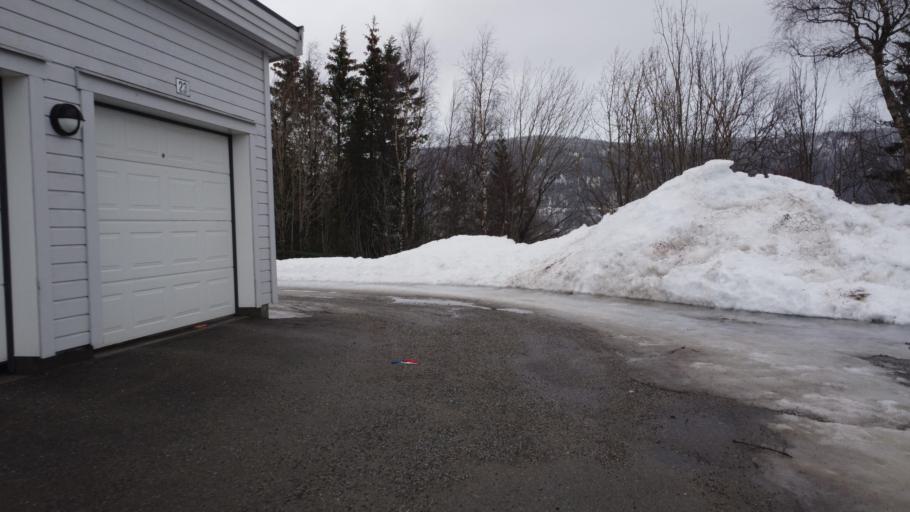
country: NO
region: Nordland
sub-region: Rana
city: Mo i Rana
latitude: 66.3190
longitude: 14.1605
